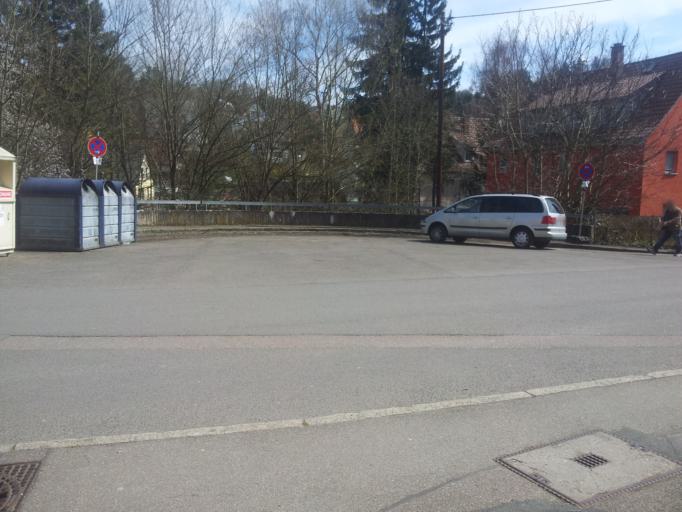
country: DE
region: Baden-Wuerttemberg
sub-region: Regierungsbezirk Stuttgart
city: Esslingen
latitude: 48.7443
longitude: 9.3272
